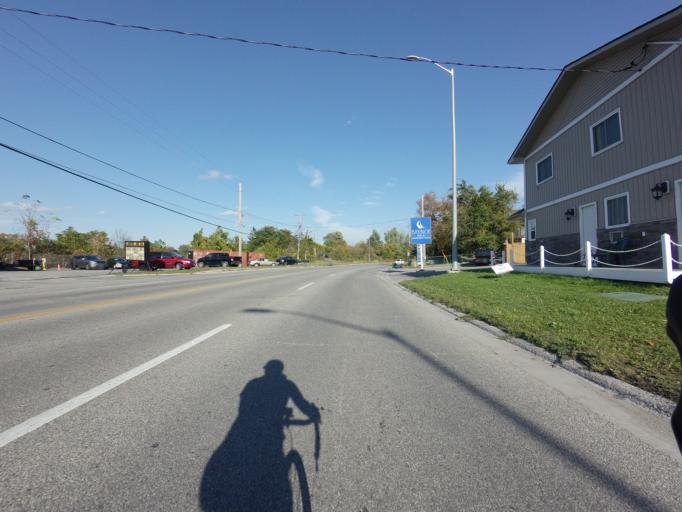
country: CA
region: Ontario
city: Kingston
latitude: 44.2421
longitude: -76.6082
